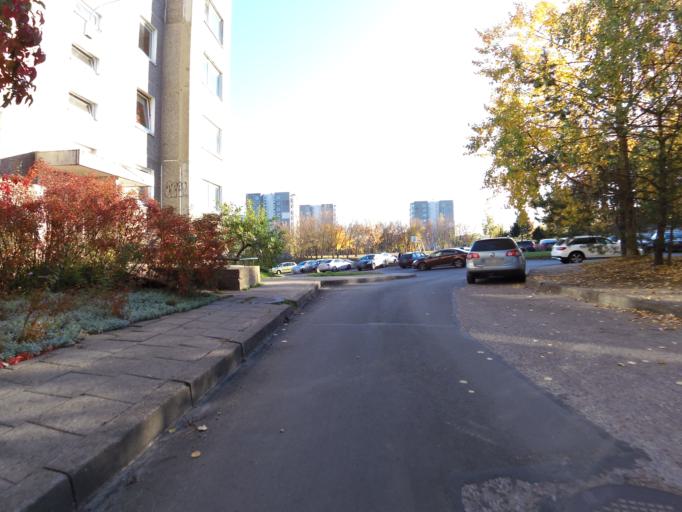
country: LT
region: Vilnius County
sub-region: Vilnius
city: Fabijoniskes
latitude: 54.7327
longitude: 25.2421
